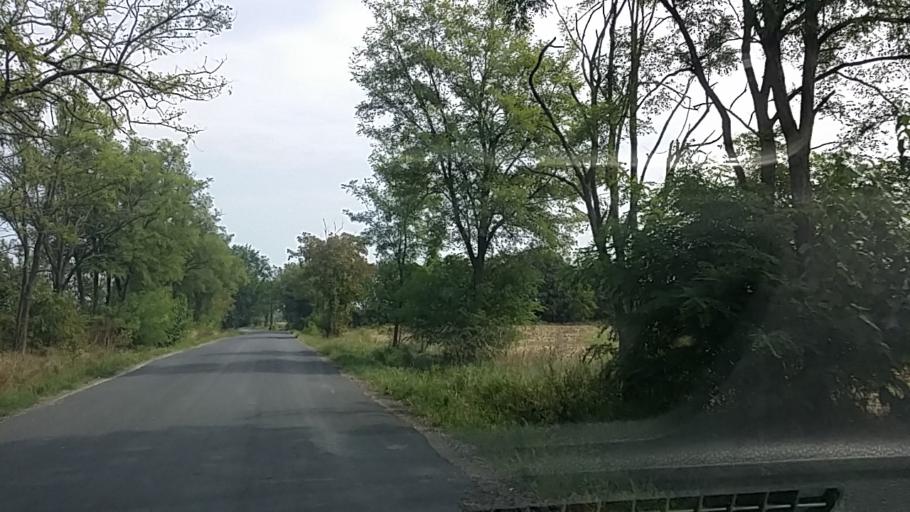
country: HU
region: Gyor-Moson-Sopron
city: Bosarkany
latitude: 47.7170
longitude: 17.2861
